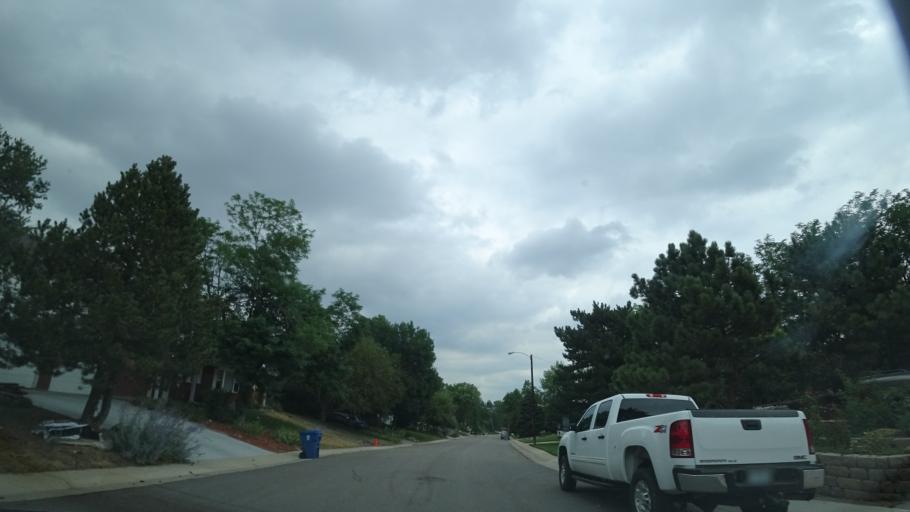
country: US
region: Colorado
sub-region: Jefferson County
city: West Pleasant View
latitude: 39.6992
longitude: -105.1527
